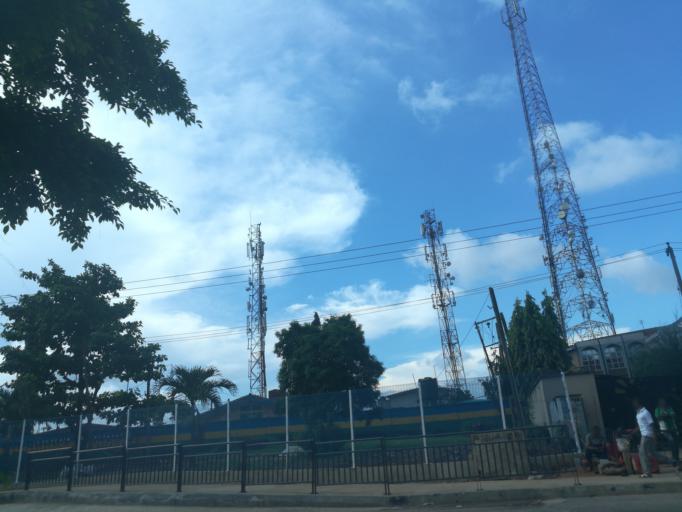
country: NG
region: Lagos
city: Ikeja
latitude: 6.6183
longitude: 3.3618
